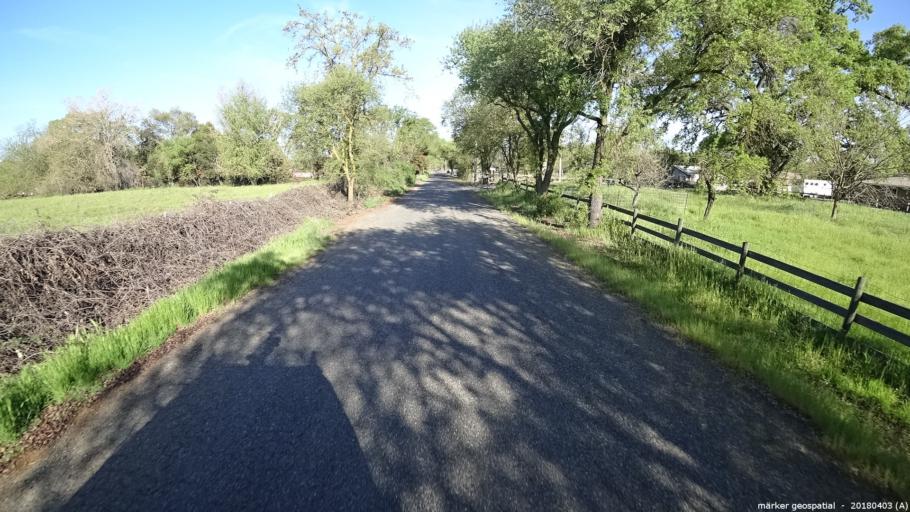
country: US
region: California
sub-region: Sacramento County
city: Wilton
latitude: 38.4354
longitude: -121.2015
